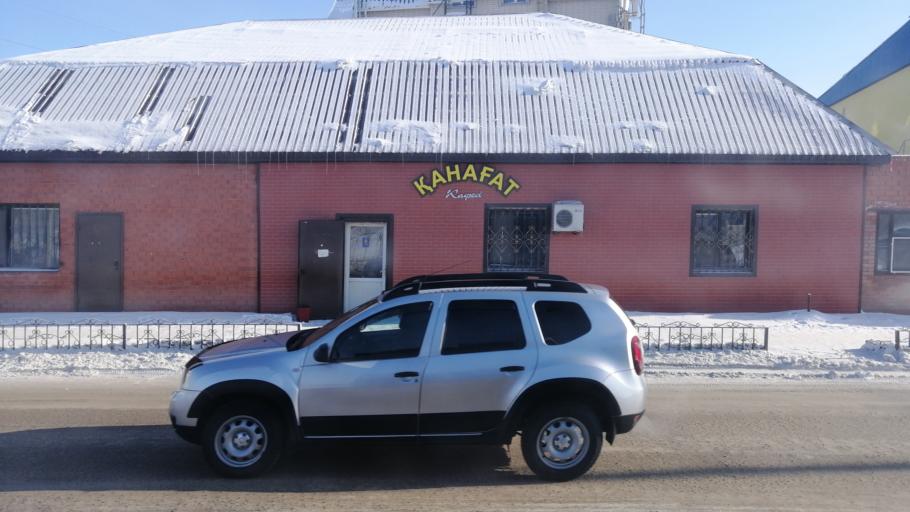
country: KZ
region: Aqtoebe
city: Aqtobe
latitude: 50.2955
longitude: 57.1980
